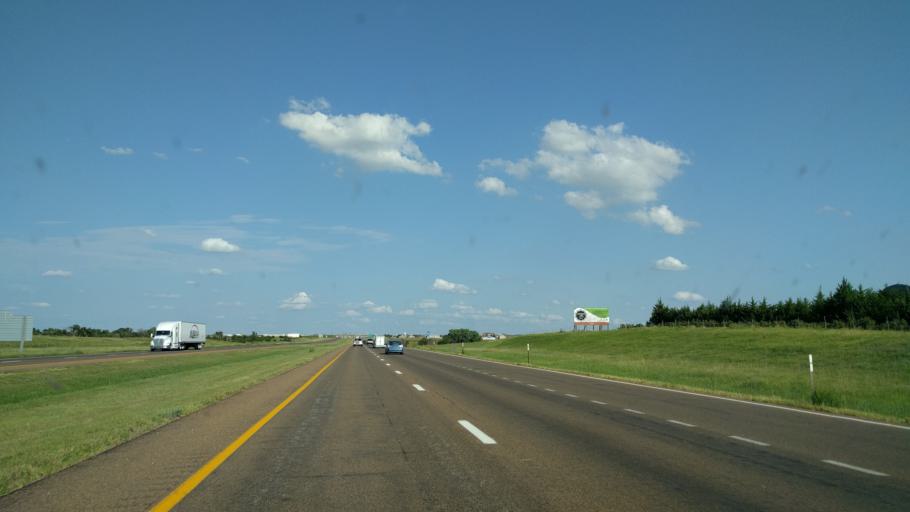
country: US
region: Kansas
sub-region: Ellis County
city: Hays
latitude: 38.9111
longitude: -99.3513
